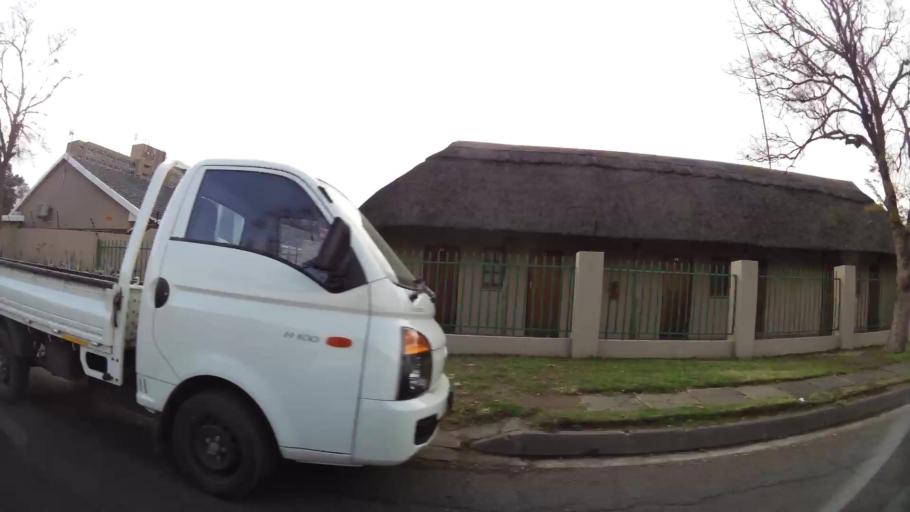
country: ZA
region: Orange Free State
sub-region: Mangaung Metropolitan Municipality
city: Bloemfontein
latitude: -29.1181
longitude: 26.1853
